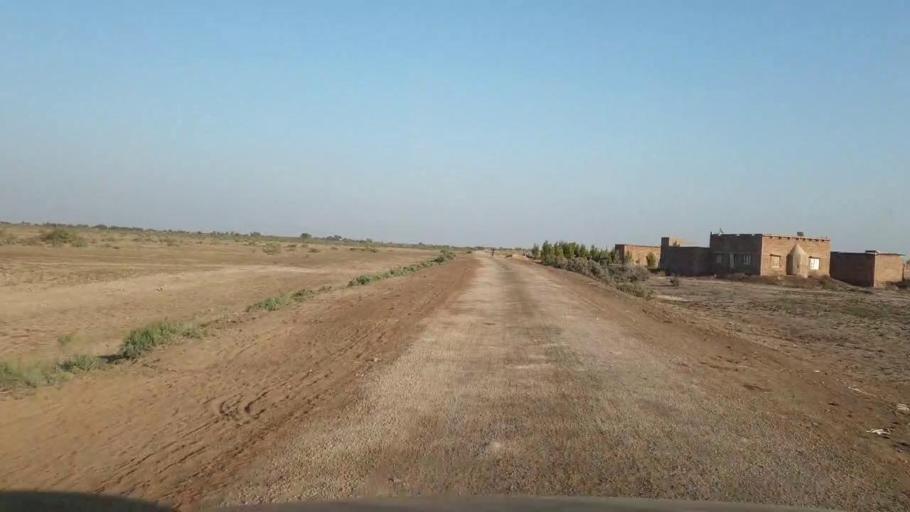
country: PK
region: Sindh
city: Samaro
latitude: 25.1204
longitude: 69.2989
